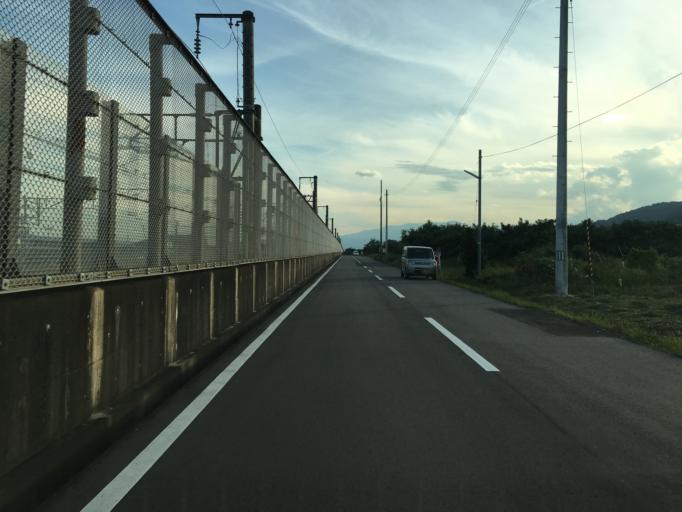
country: JP
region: Fukushima
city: Hobaramachi
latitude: 37.8555
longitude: 140.5172
